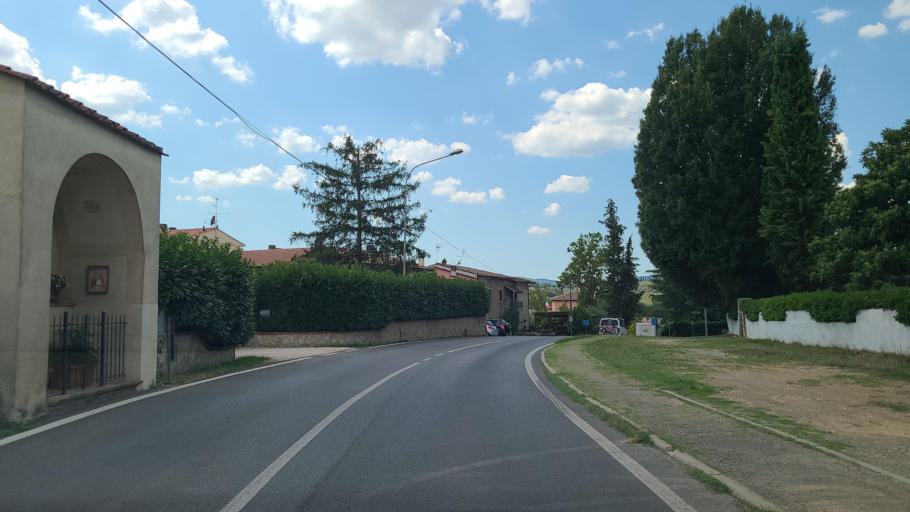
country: IT
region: Tuscany
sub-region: Provincia di Siena
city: Colle di Val d'Elsa
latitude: 43.4138
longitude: 11.0777
